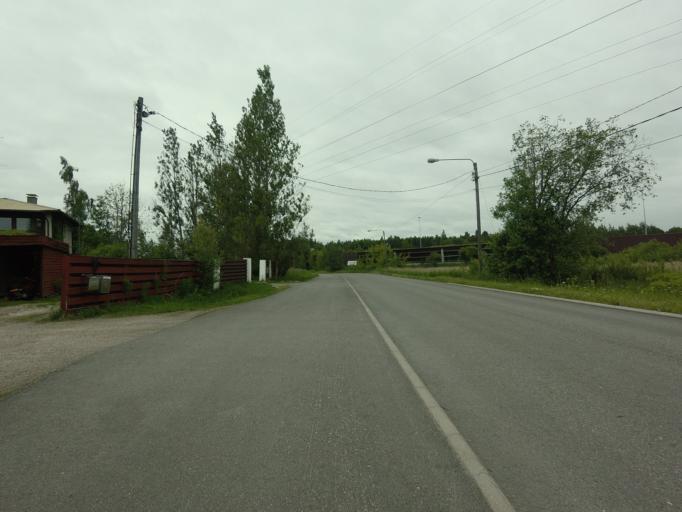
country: FI
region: Uusimaa
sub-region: Helsinki
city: Koukkuniemi
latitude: 60.1794
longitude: 24.7514
